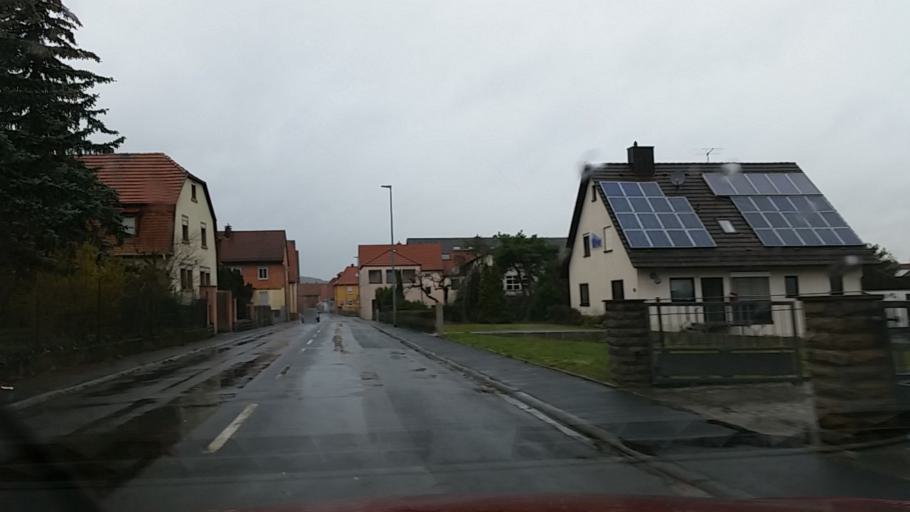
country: DE
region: Bavaria
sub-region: Regierungsbezirk Unterfranken
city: Zellingen
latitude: 49.8951
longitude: 9.8207
